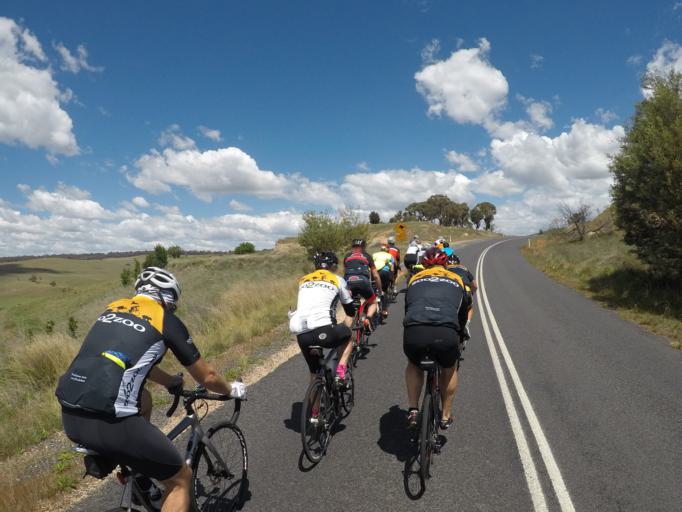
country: AU
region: New South Wales
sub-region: Blayney
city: Blayney
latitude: -33.5786
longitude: 149.4043
